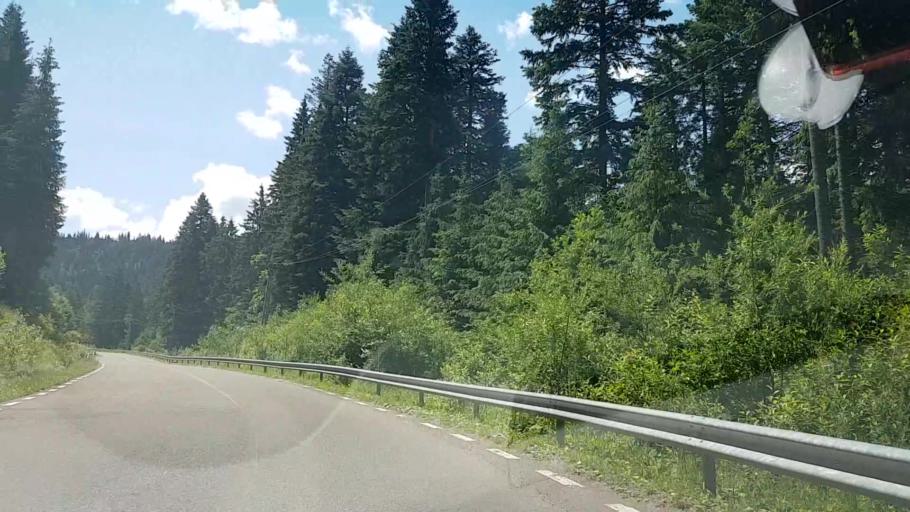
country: RO
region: Suceava
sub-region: Comuna Sadova
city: Sadova
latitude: 47.4713
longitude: 25.5123
